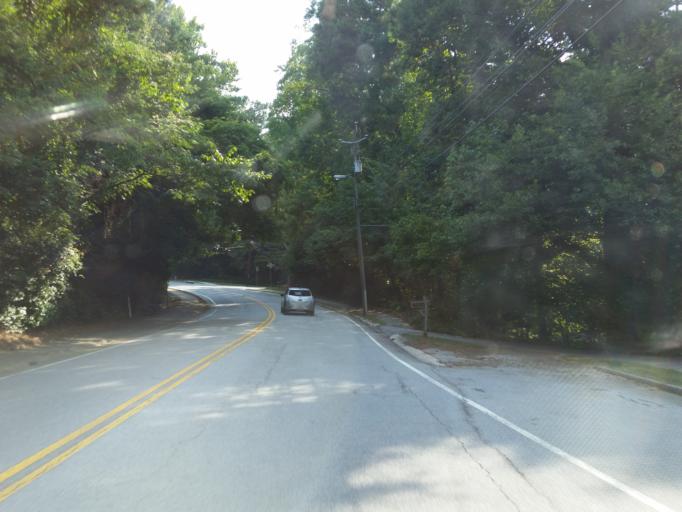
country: US
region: Georgia
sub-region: DeKalb County
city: North Atlanta
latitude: 33.8826
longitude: -84.3560
